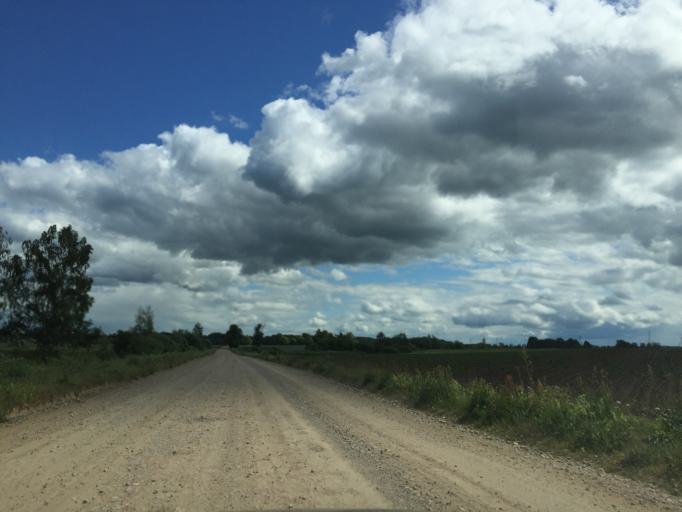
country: LV
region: Lecava
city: Iecava
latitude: 56.5063
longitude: 24.3519
